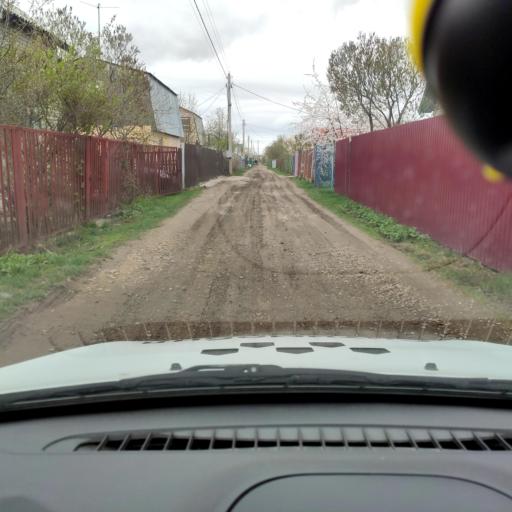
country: RU
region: Samara
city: Tol'yatti
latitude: 53.5830
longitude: 49.3159
